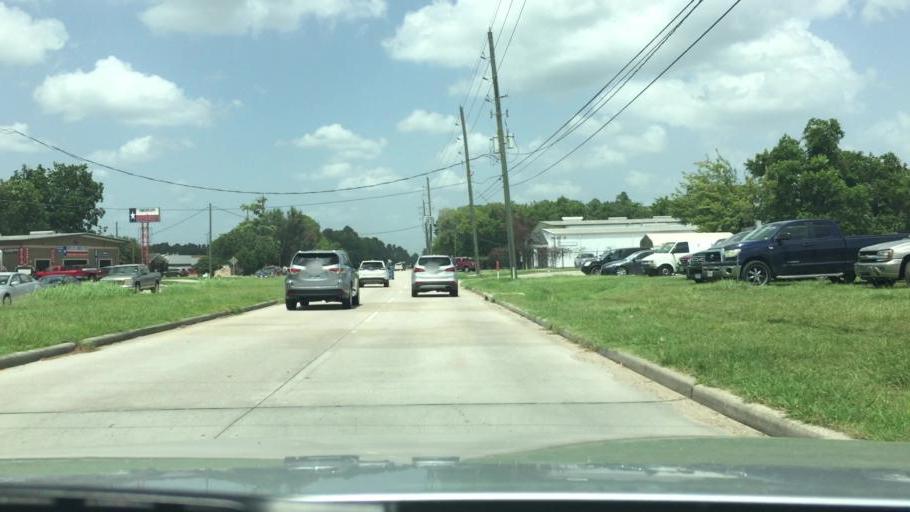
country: US
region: Texas
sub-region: Harris County
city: Hudson
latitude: 29.9628
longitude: -95.5293
